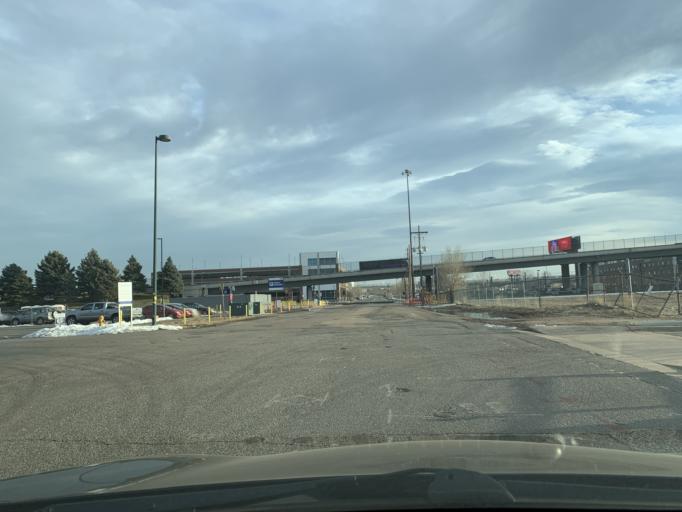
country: US
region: Colorado
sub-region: Denver County
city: Denver
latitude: 39.7448
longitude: -105.0124
